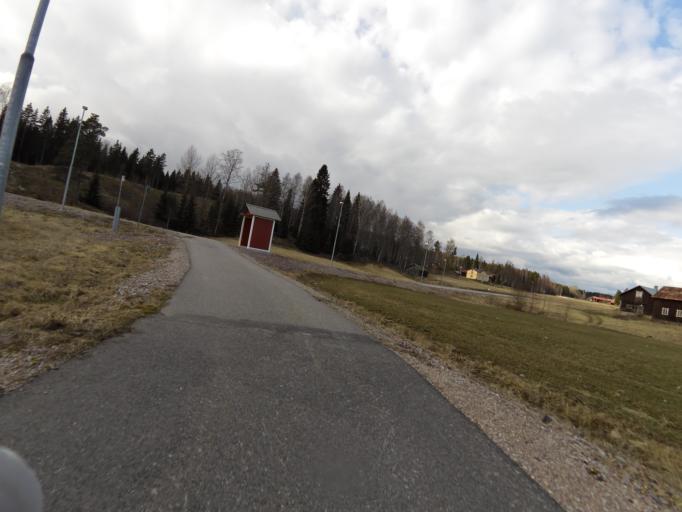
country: SE
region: Dalarna
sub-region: Avesta Kommun
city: Horndal
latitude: 60.4499
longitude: 16.4498
